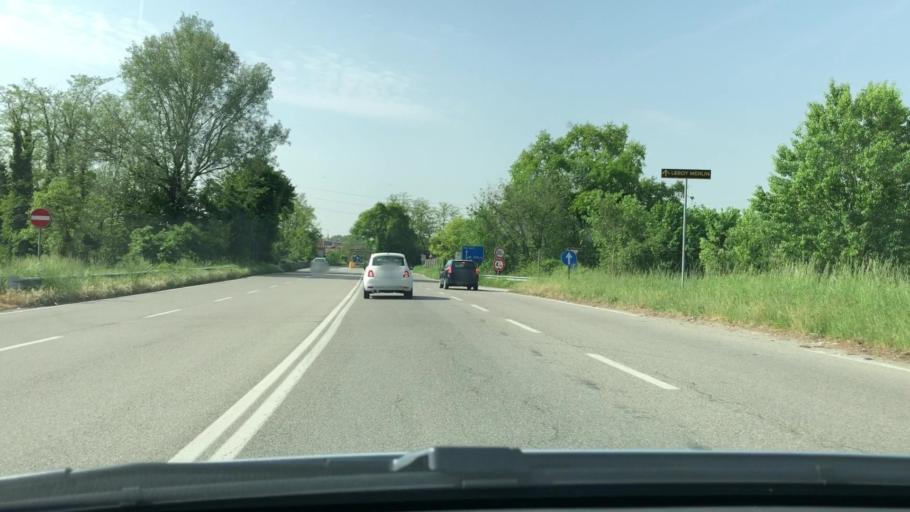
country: IT
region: Lombardy
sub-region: Provincia di Monza e Brianza
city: Meda
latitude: 45.6551
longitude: 9.1548
